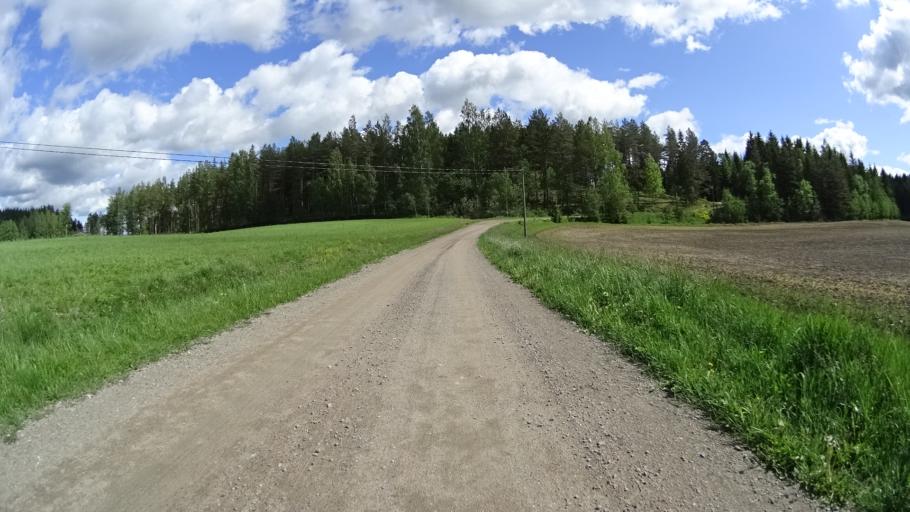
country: FI
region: Uusimaa
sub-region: Raaseporin
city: Pohja
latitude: 60.1231
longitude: 23.5863
